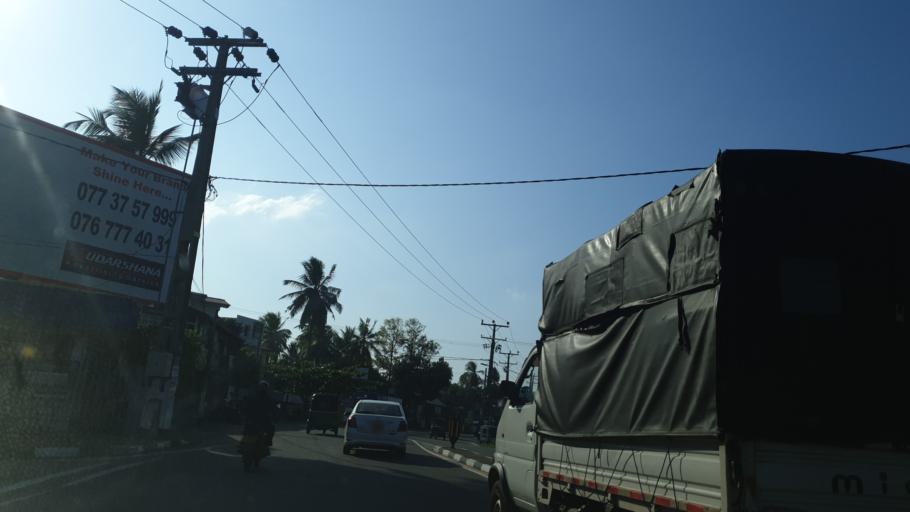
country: LK
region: Western
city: Sri Jayewardenepura Kotte
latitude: 6.8769
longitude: 79.9268
